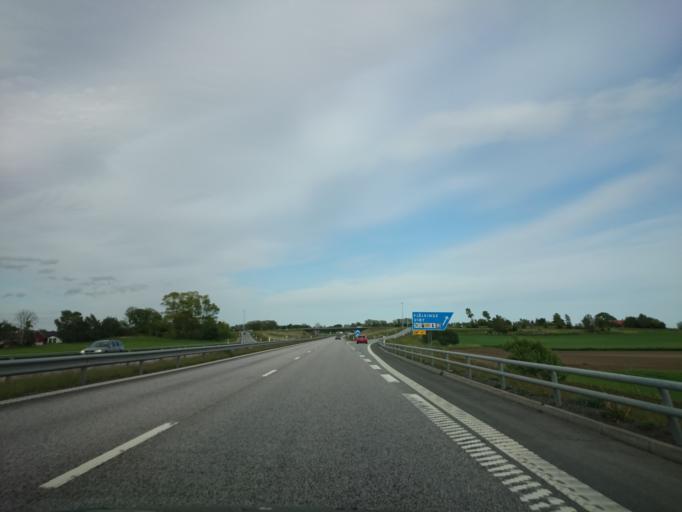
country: SE
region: Skane
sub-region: Kristianstads Kommun
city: Fjalkinge
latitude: 56.0331
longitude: 14.2564
